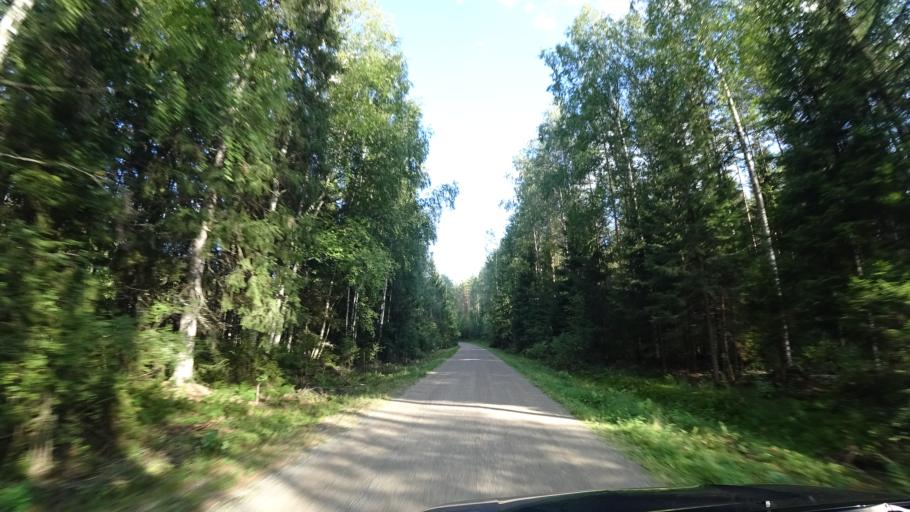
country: FI
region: Paijanne Tavastia
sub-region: Lahti
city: Auttoinen
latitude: 61.2147
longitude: 25.1563
